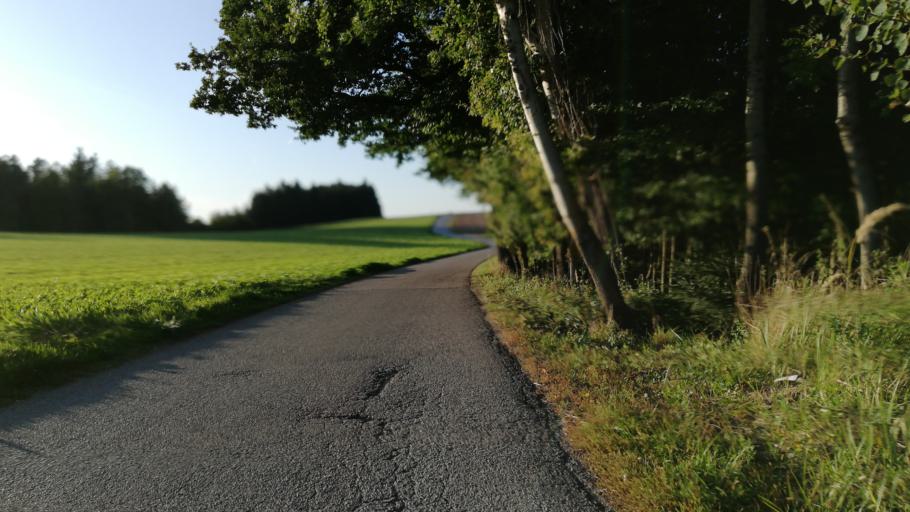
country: AT
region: Upper Austria
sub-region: Wels-Land
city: Pennewang
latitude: 48.1613
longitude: 13.8617
